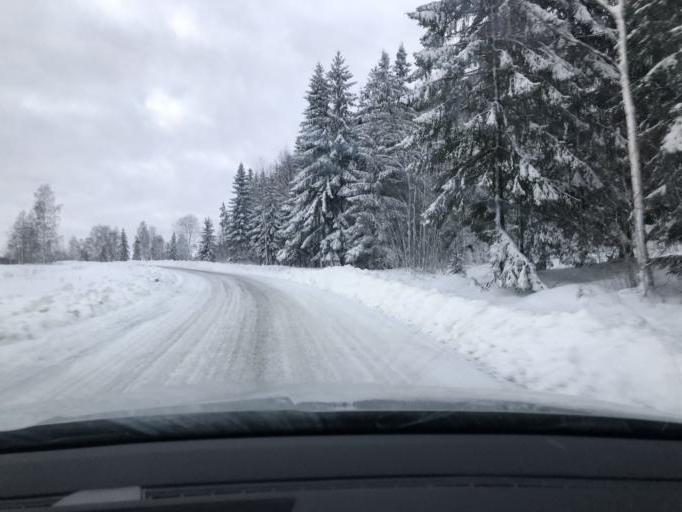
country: SE
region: Vaesternorrland
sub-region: Kramfors Kommun
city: Nordingra
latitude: 62.9166
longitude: 18.2326
